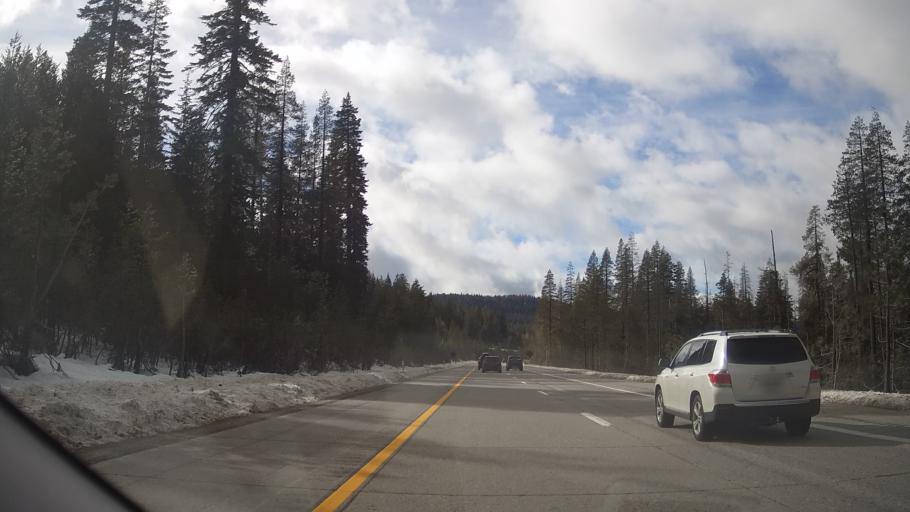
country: US
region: California
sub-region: Nevada County
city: Truckee
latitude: 39.3180
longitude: -120.4318
